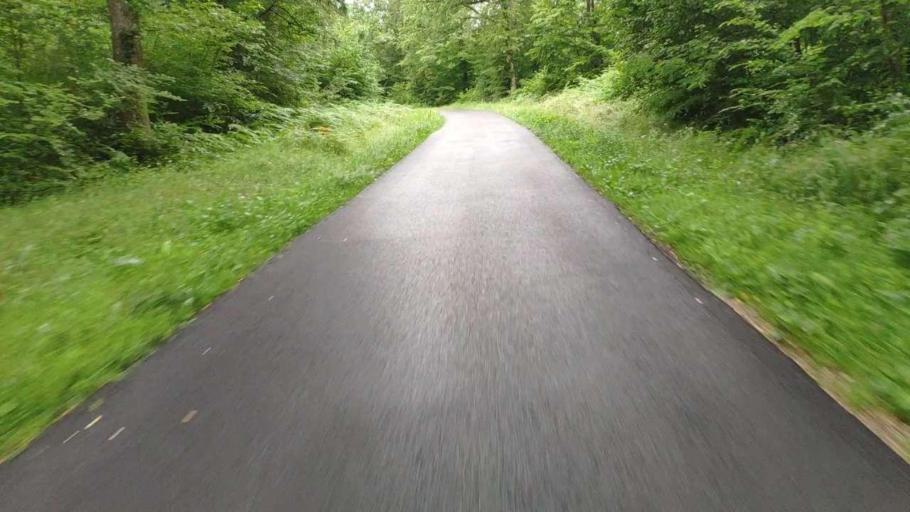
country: FR
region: Franche-Comte
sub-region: Departement du Jura
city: Chaussin
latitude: 46.8888
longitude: 5.4260
